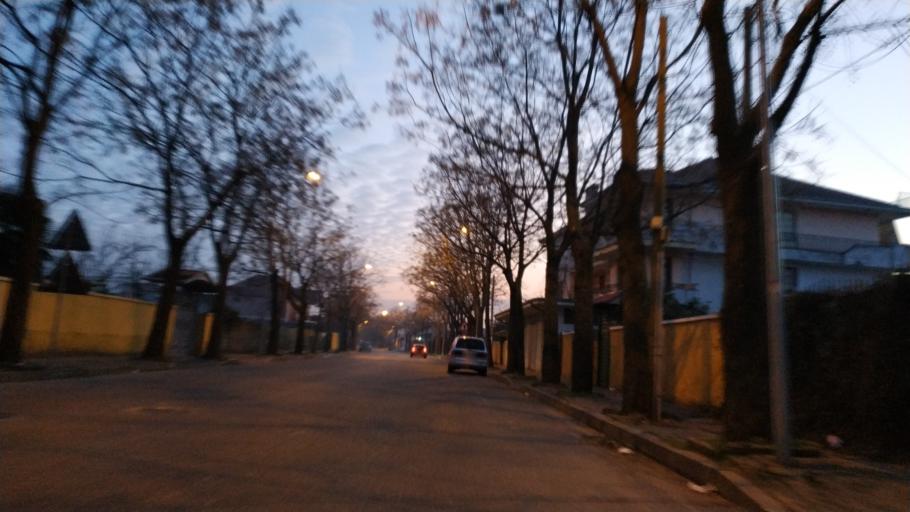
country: AL
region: Shkoder
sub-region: Rrethi i Shkodres
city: Shkoder
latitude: 42.0751
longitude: 19.5028
